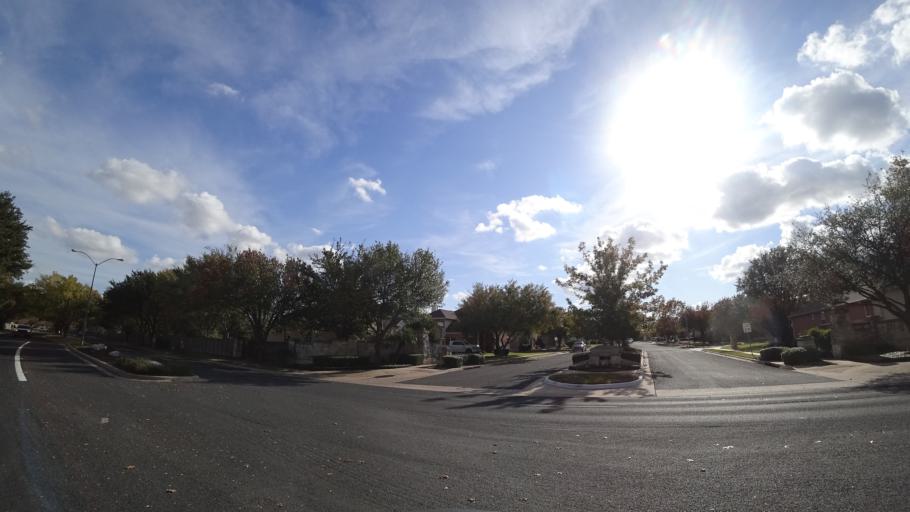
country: US
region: Texas
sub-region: Williamson County
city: Brushy Creek
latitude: 30.5054
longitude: -97.7365
